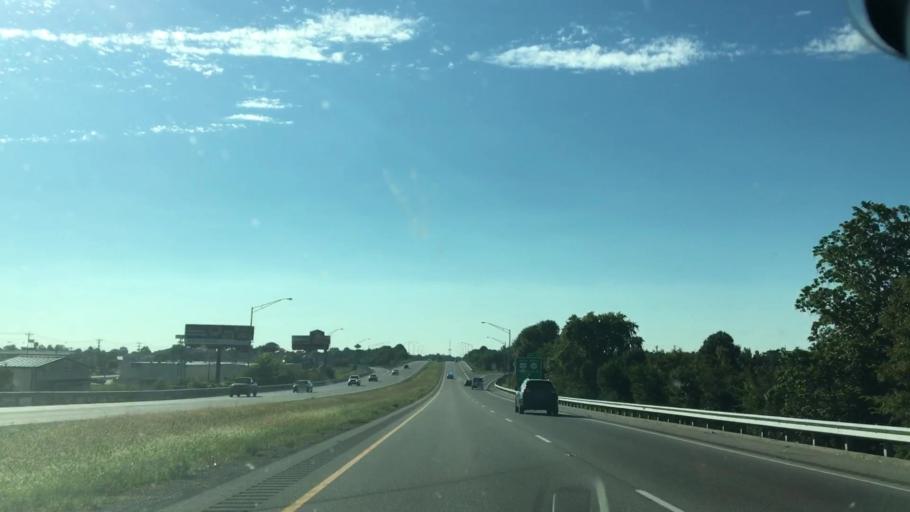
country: US
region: Kentucky
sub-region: Daviess County
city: Owensboro
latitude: 37.7272
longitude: -87.1158
